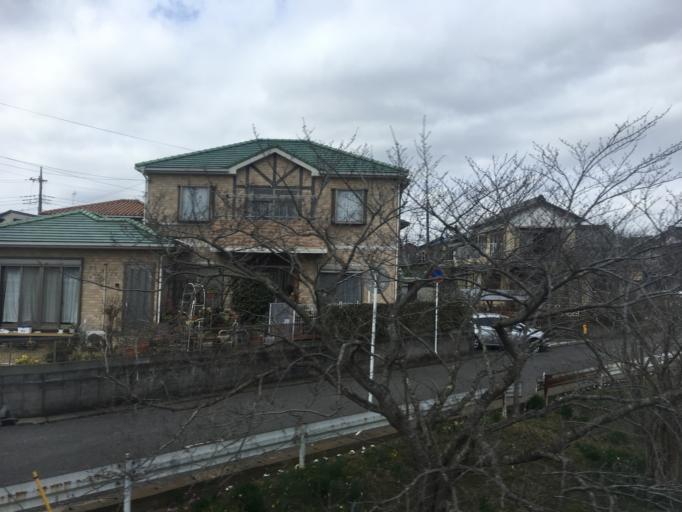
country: JP
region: Chiba
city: Shisui
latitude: 35.7341
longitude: 140.2769
